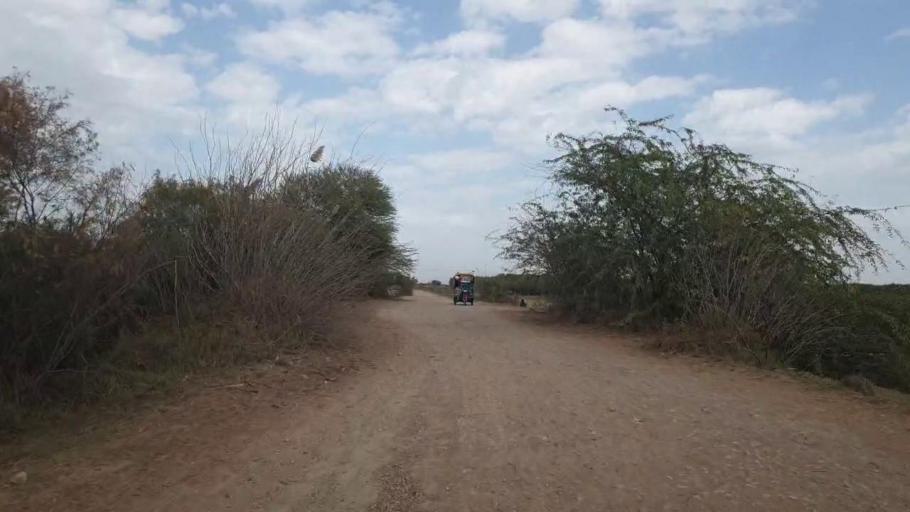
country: PK
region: Sindh
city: Hala
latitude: 25.9550
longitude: 68.4629
